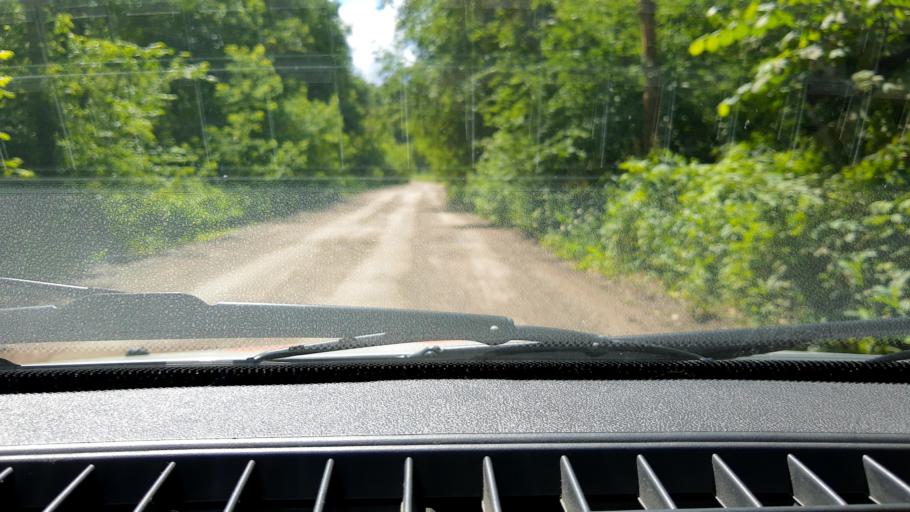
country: RU
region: Bashkortostan
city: Ufa
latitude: 54.6879
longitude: 56.0540
